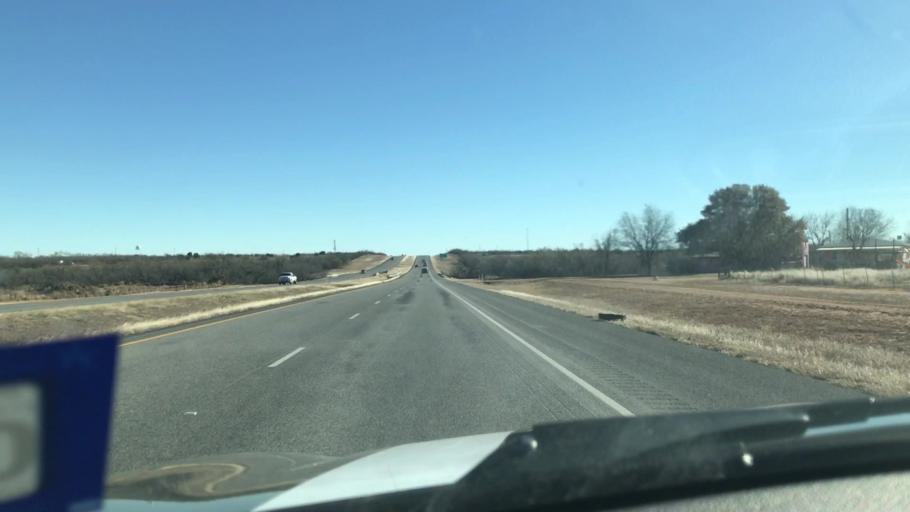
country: US
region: Texas
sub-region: Scurry County
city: Snyder
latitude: 32.7645
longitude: -100.9343
